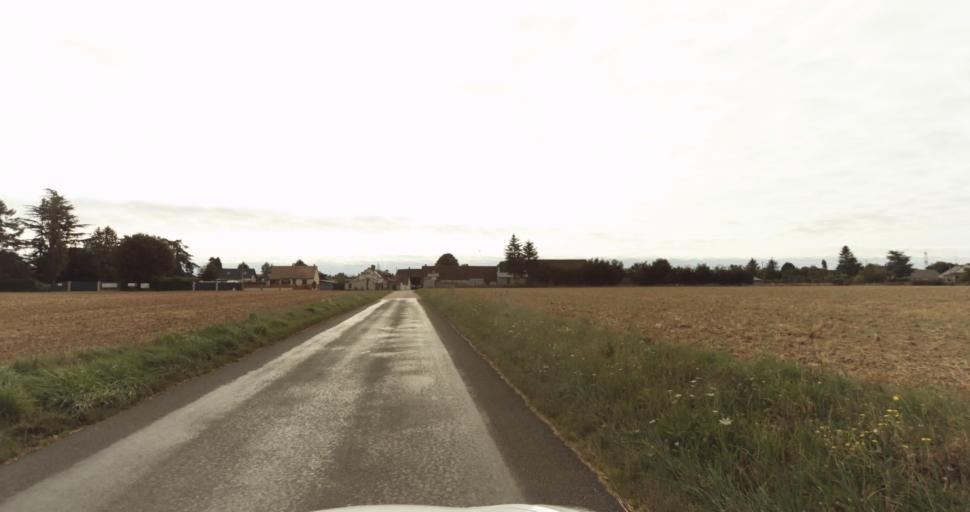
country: FR
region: Haute-Normandie
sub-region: Departement de l'Eure
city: La Madeleine-de-Nonancourt
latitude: 48.8644
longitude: 1.2426
